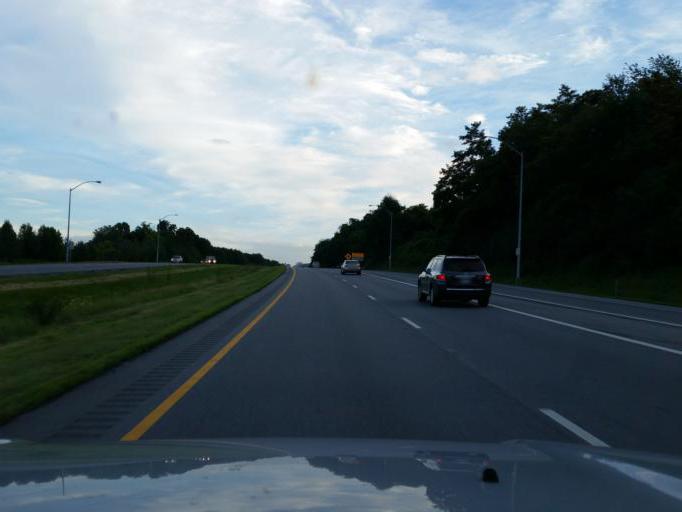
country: US
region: Maryland
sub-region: Frederick County
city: Thurmont
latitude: 39.6125
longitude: -77.4219
